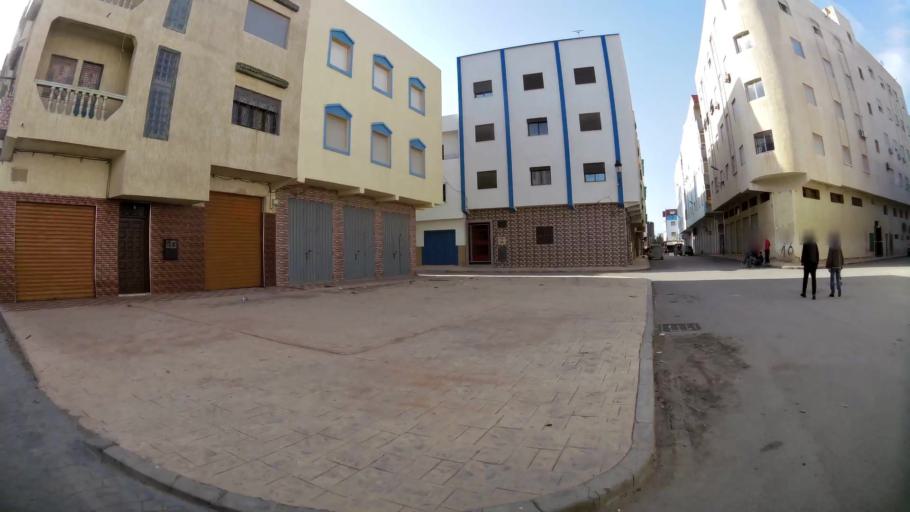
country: MA
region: Tanger-Tetouan
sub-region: Tetouan
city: Martil
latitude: 35.6136
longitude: -5.2804
